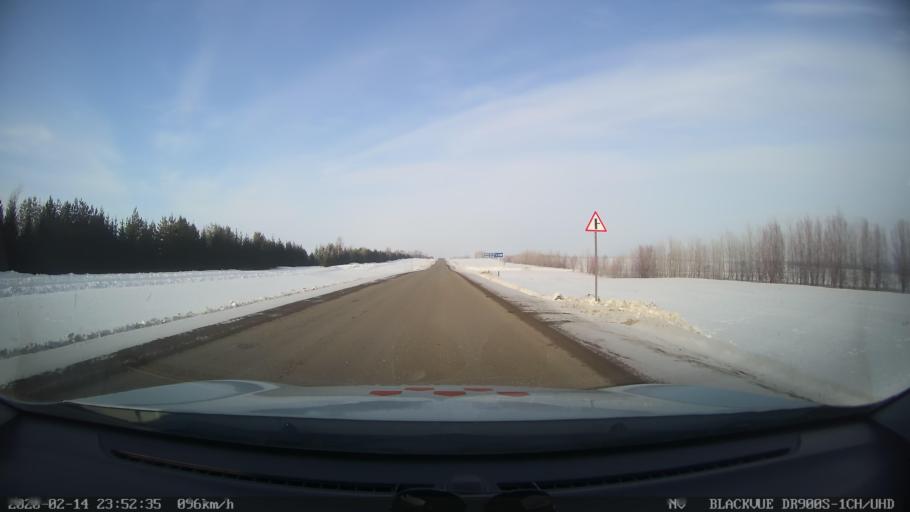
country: RU
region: Tatarstan
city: Kuybyshevskiy Zaton
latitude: 55.2808
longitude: 49.1438
